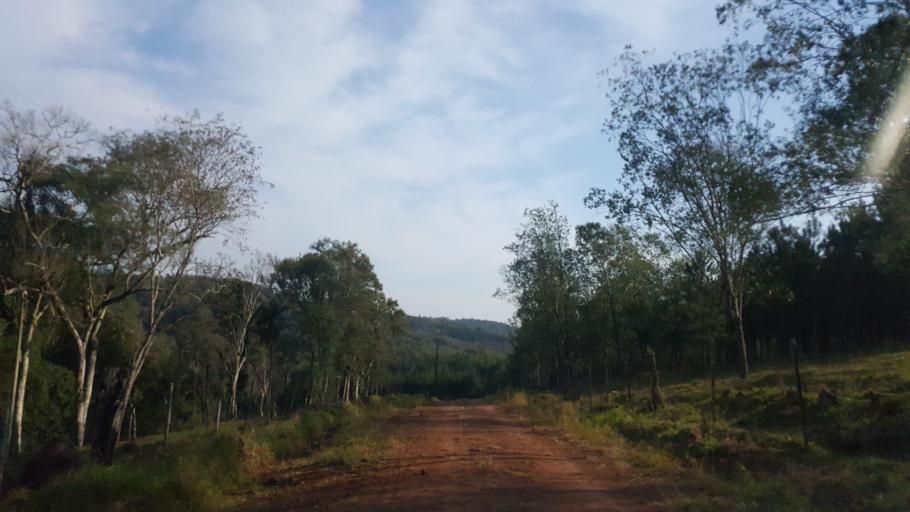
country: AR
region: Misiones
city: Capiovi
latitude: -26.9057
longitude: -55.0905
